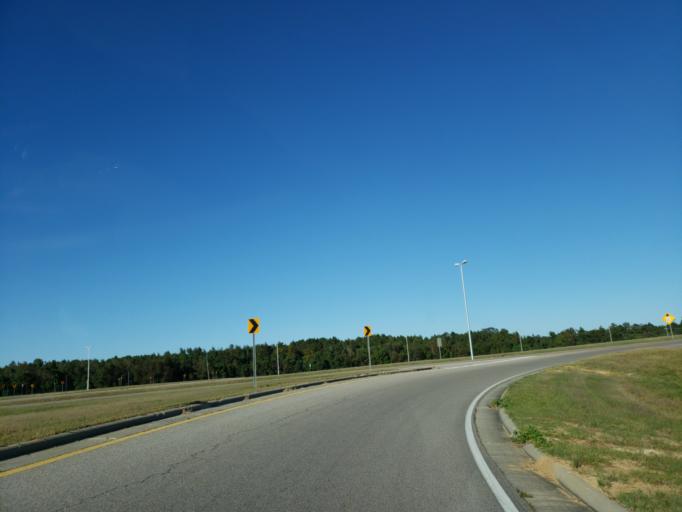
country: US
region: Mississippi
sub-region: Forrest County
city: Petal
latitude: 31.3589
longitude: -89.2747
